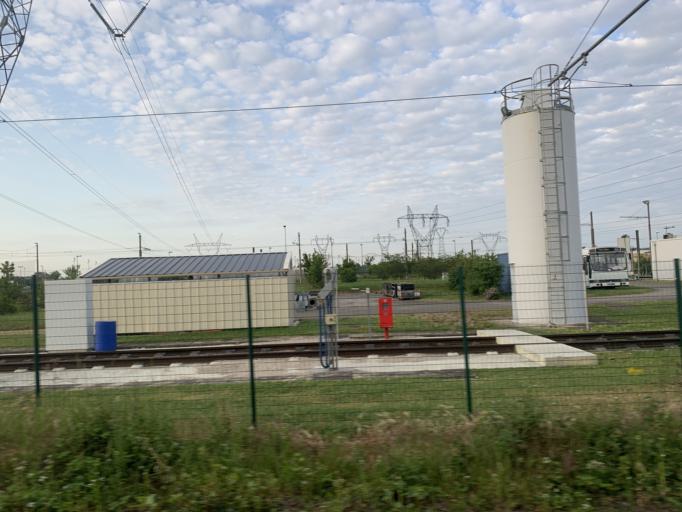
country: FR
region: Rhone-Alpes
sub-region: Departement du Rhone
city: Jonage
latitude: 45.7673
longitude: 5.0339
